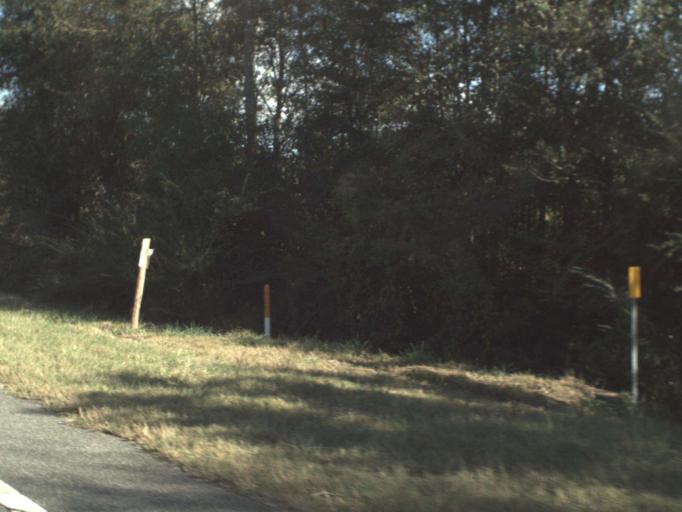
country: US
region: Florida
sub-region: Washington County
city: Chipley
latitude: 30.7834
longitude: -85.4809
